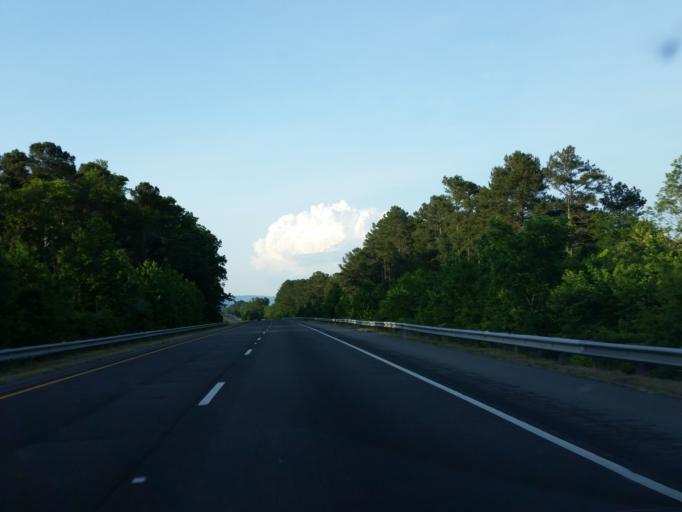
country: US
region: Alabama
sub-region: DeKalb County
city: Henagar
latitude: 34.6264
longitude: -85.6251
